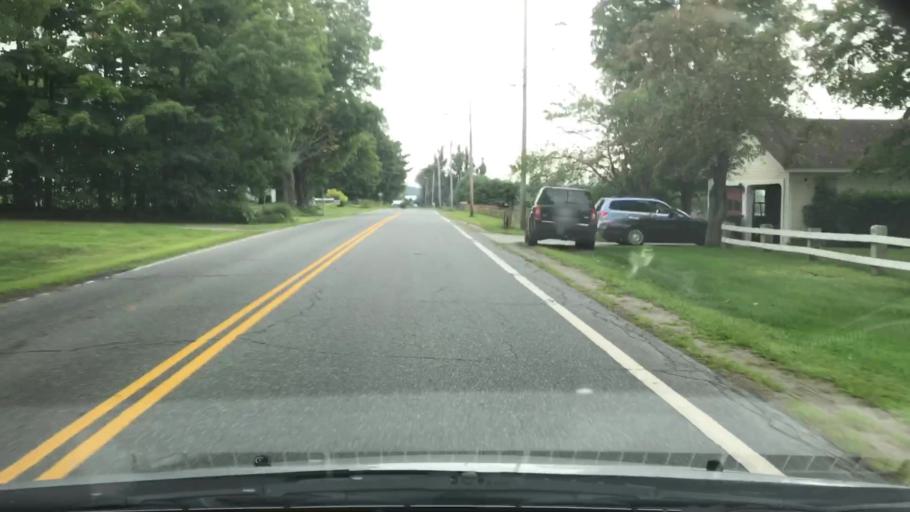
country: US
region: New Hampshire
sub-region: Grafton County
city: Haverhill
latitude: 44.0299
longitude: -72.0666
